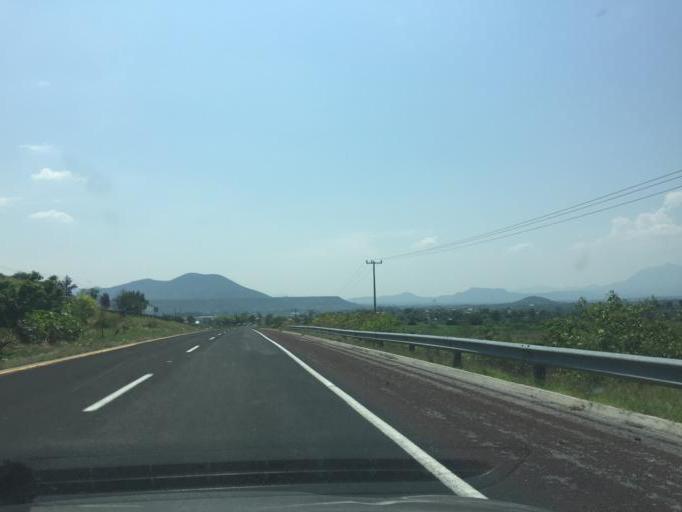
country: MX
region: Hidalgo
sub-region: Ixmiquilpan
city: Taxadho
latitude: 20.4233
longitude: -99.1344
